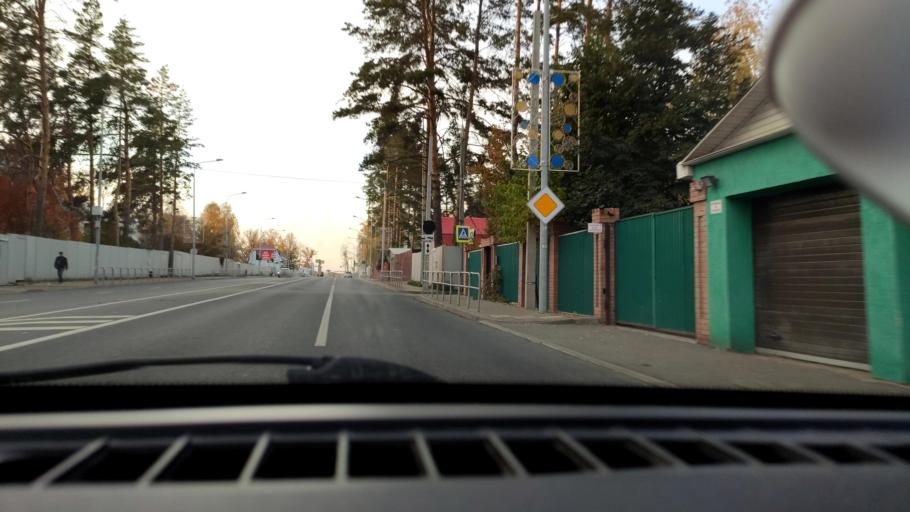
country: RU
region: Samara
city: Samara
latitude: 53.2652
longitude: 50.2431
